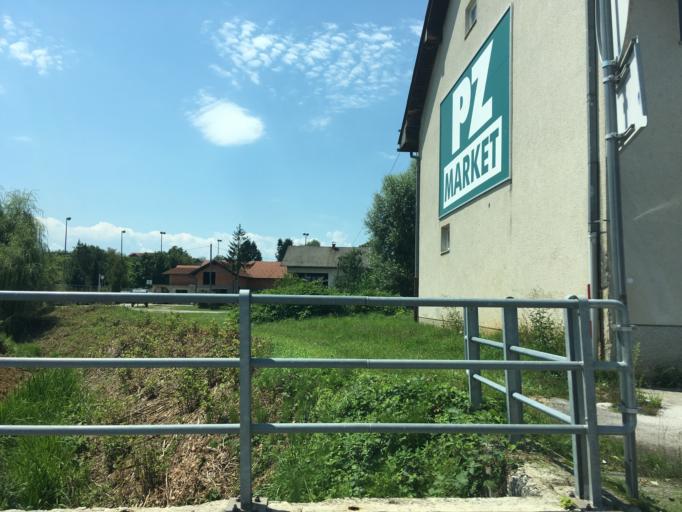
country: SI
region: Metlika
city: Metlika
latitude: 45.6329
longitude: 15.3234
